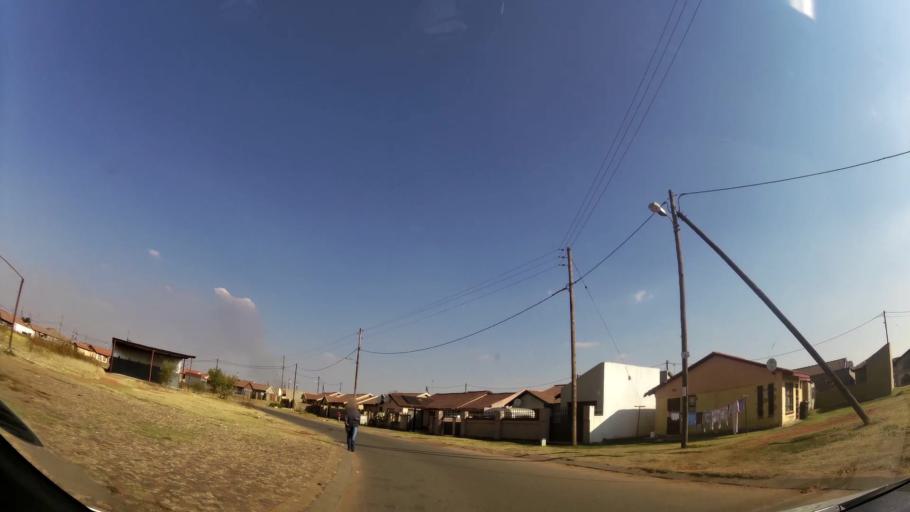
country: ZA
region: Gauteng
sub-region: Ekurhuleni Metropolitan Municipality
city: Benoni
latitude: -26.2274
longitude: 28.3265
